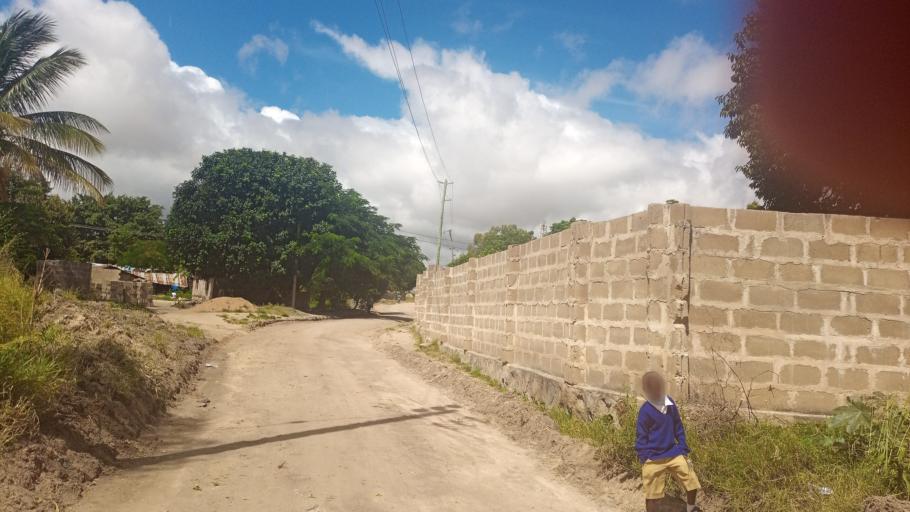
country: TZ
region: Dodoma
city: Dodoma
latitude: -6.1945
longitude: 35.7269
